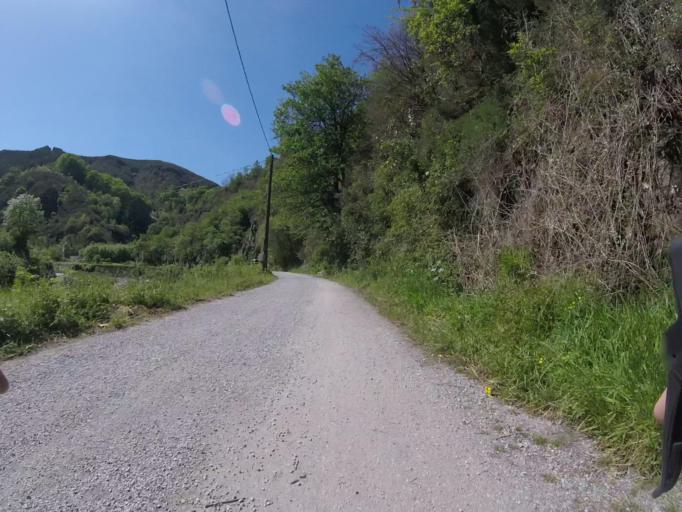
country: ES
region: Navarre
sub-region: Provincia de Navarra
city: Bera
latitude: 43.2931
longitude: -1.7299
